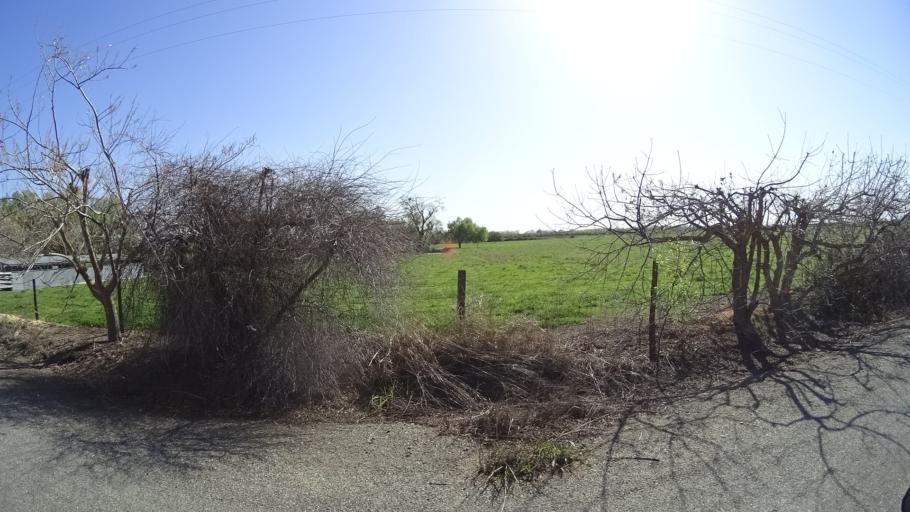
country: US
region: California
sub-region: Glenn County
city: Hamilton City
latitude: 39.7805
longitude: -122.0477
